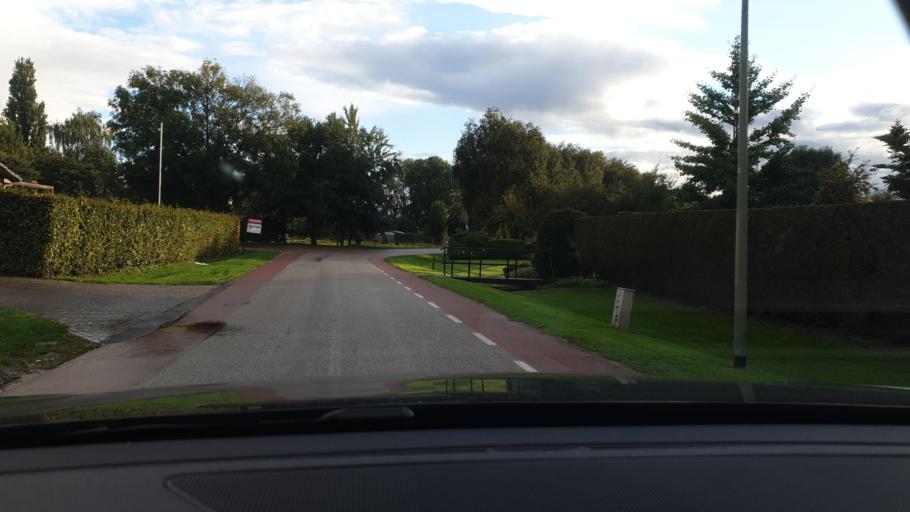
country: NL
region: North Brabant
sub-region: Gemeente Landerd
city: Schaijk
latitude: 51.7901
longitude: 5.6463
